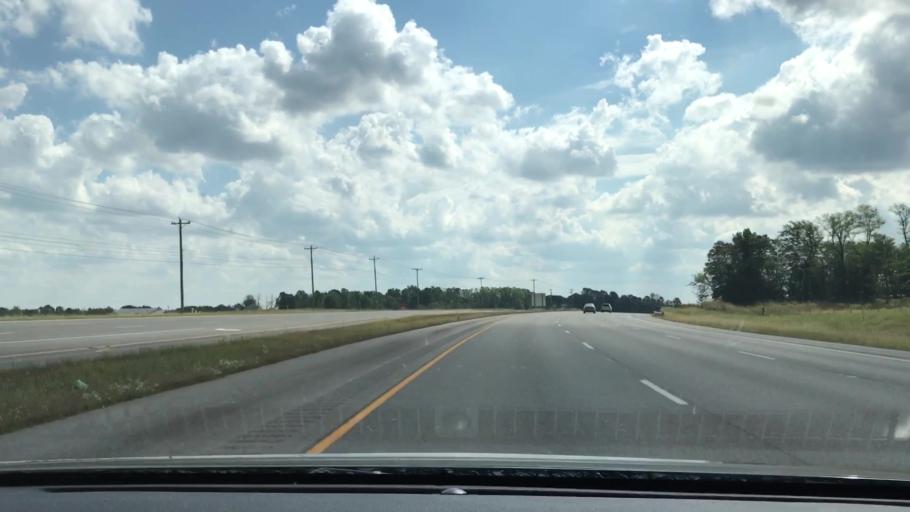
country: US
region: Kentucky
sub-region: Christian County
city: Oak Grove
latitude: 36.6851
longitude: -87.4499
